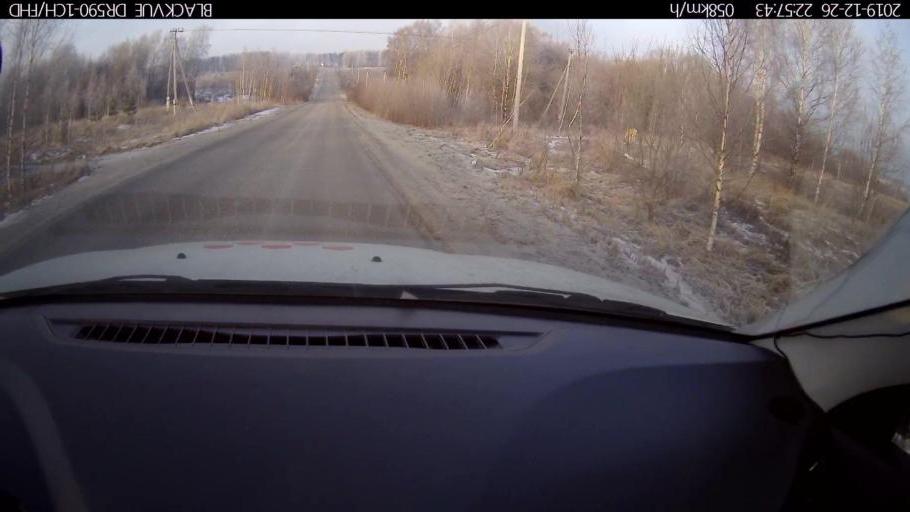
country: RU
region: Nizjnij Novgorod
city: Burevestnik
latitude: 56.1526
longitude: 43.7138
